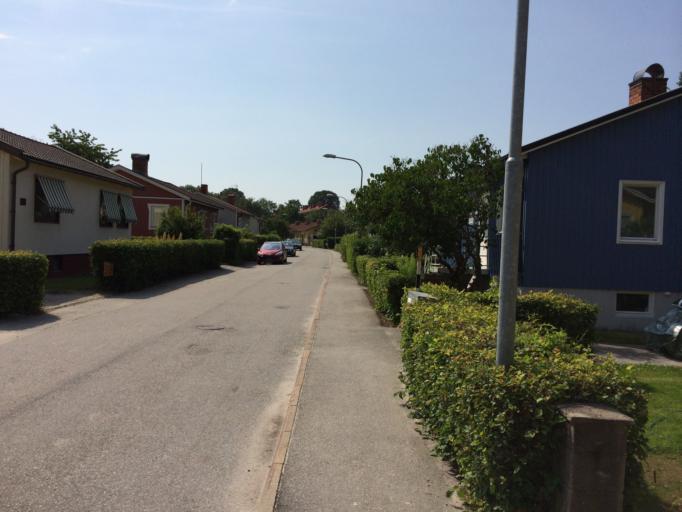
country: SE
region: Stockholm
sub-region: Huddinge Kommun
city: Huddinge
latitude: 59.2931
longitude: 17.9886
